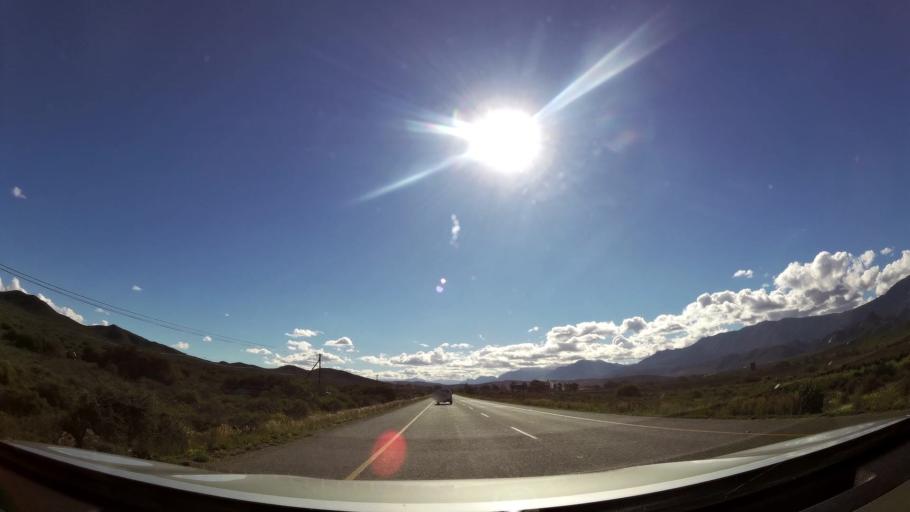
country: ZA
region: Western Cape
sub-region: Cape Winelands District Municipality
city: Ashton
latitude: -33.7689
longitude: 19.7482
